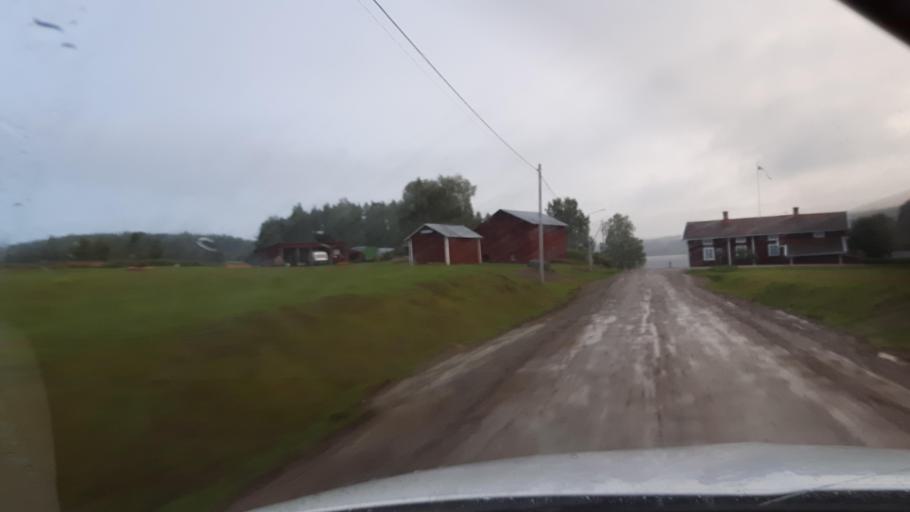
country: SE
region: Vaesternorrland
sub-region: Ange Kommun
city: Ange
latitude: 62.1472
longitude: 15.6672
